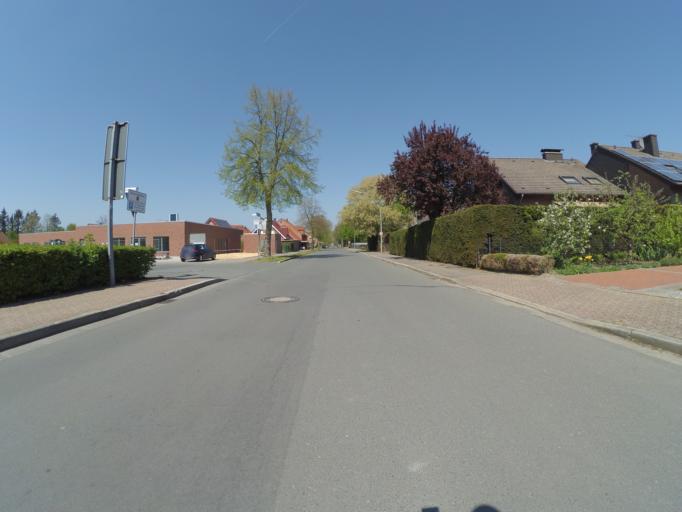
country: DE
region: North Rhine-Westphalia
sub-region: Regierungsbezirk Munster
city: Nordkirchen
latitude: 51.7417
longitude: 7.5278
